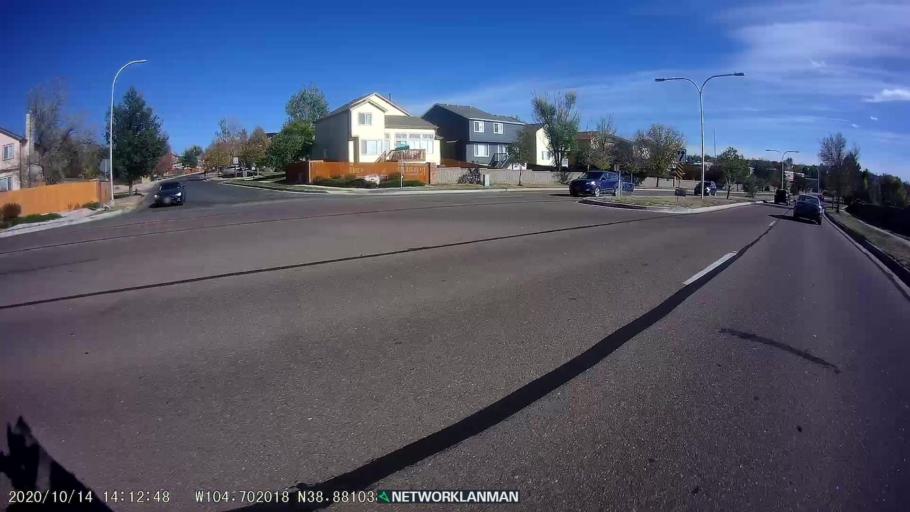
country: US
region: Colorado
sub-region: El Paso County
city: Cimarron Hills
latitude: 38.8810
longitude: -104.7016
